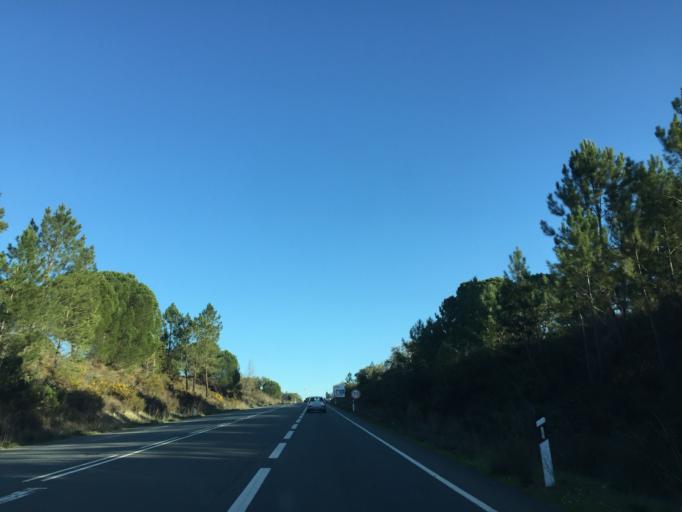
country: PT
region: Setubal
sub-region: Grandola
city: Grandola
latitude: 38.1209
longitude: -8.4277
